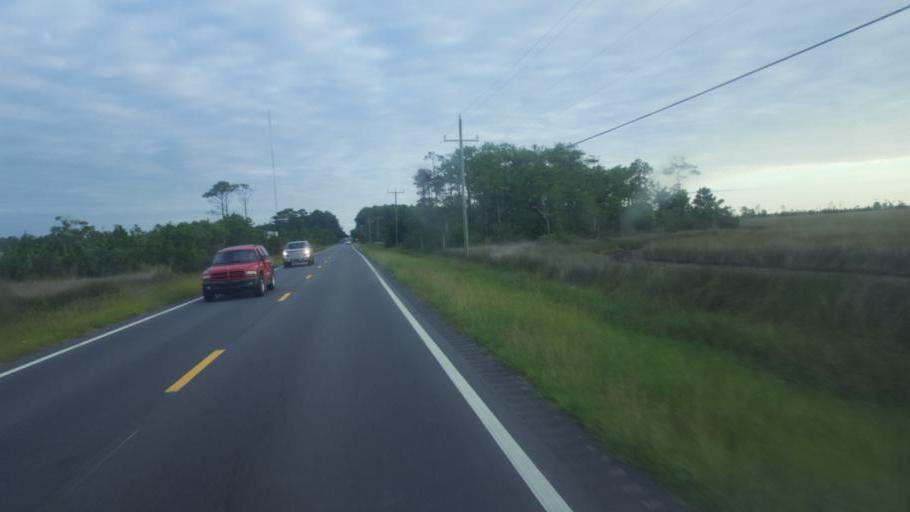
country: US
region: North Carolina
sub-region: Dare County
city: Wanchese
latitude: 35.8581
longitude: -75.6464
